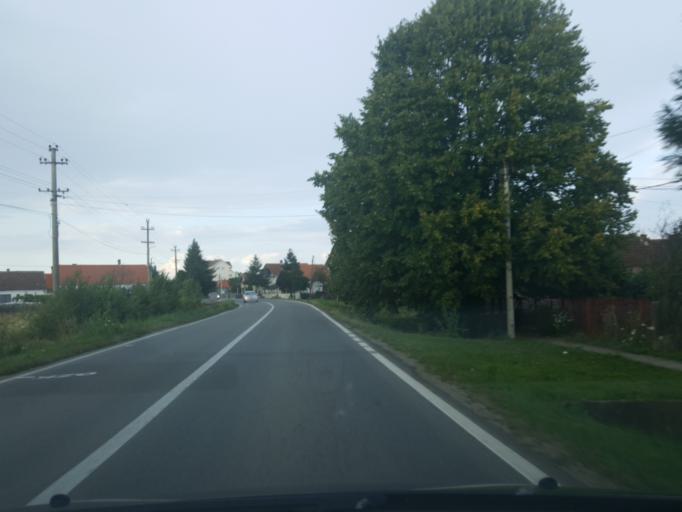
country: RS
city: Ribari
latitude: 44.7193
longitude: 19.4448
